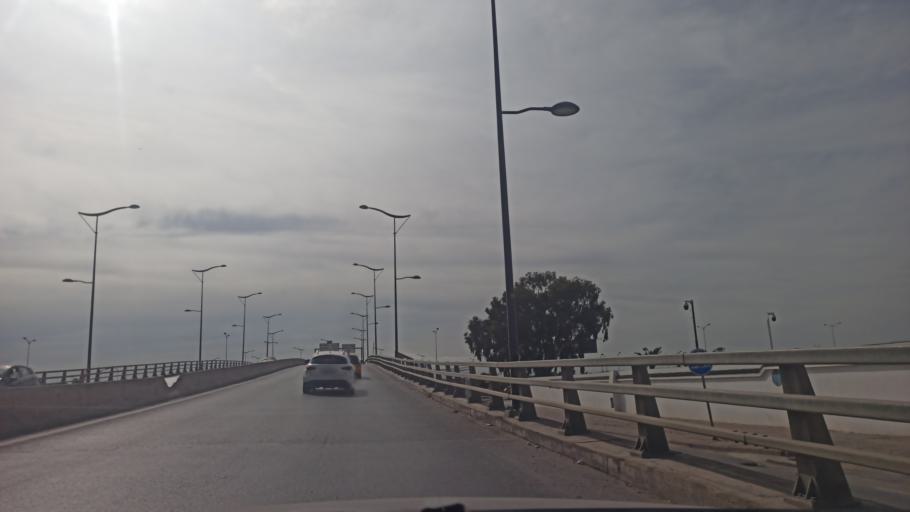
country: TN
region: Tunis
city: La Goulette
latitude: 36.8486
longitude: 10.2598
